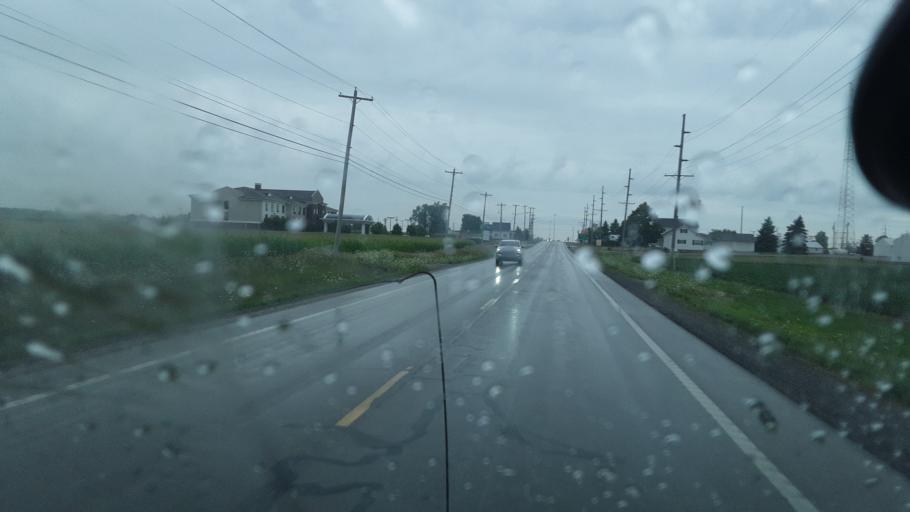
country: US
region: Ohio
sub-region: Williams County
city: Montpelier
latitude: 41.6047
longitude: -84.5558
